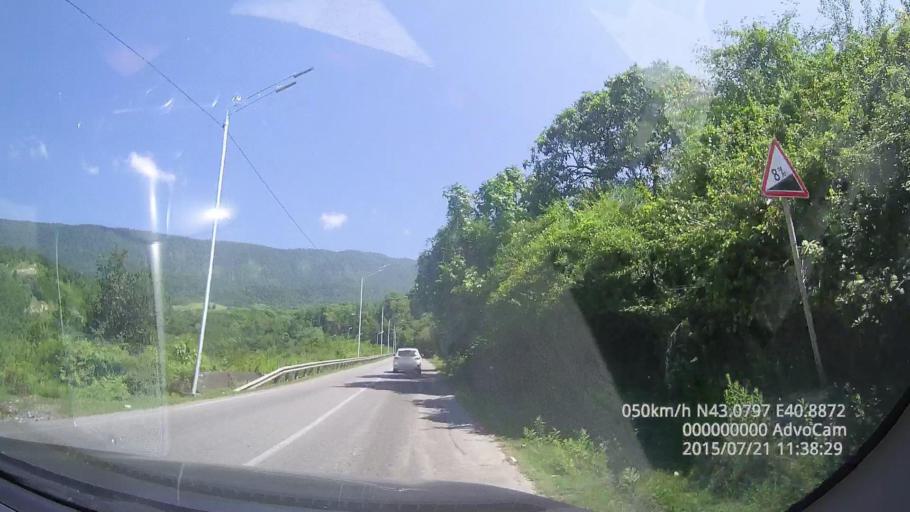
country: GE
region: Abkhazia
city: Stantsiya Novyy Afon
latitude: 43.0800
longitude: 40.8874
